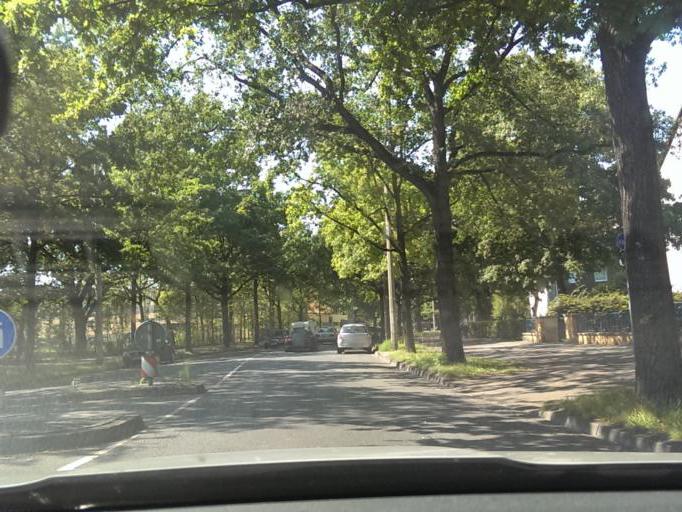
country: DE
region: Lower Saxony
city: Hannover
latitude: 52.3951
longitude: 9.7528
